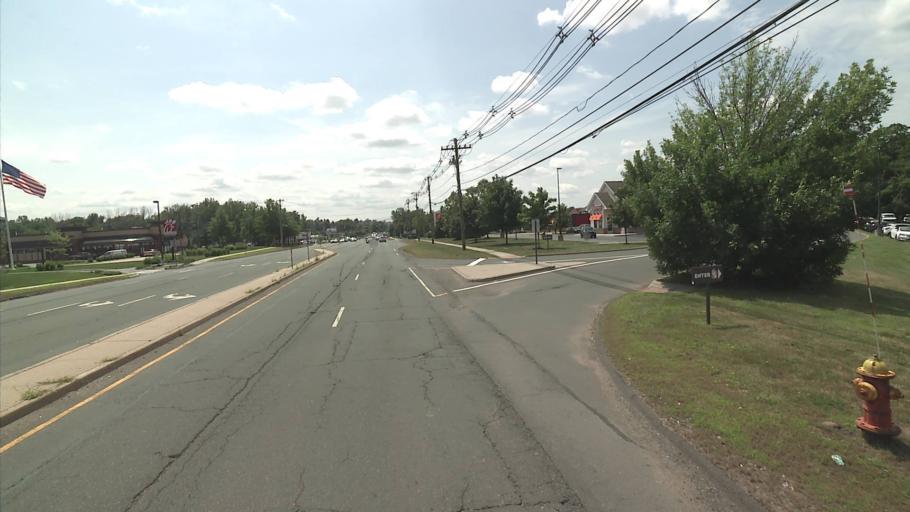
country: US
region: Connecticut
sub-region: New Haven County
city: Meriden
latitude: 41.4978
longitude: -72.8100
